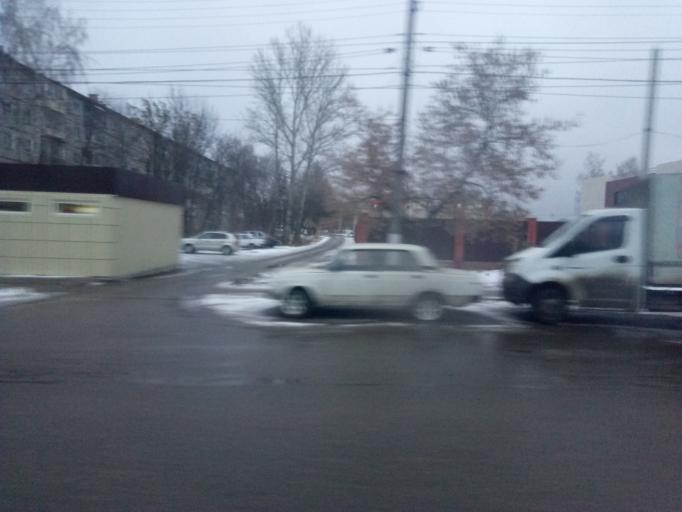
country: RU
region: Tula
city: Kosaya Gora
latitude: 54.1922
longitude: 37.5367
